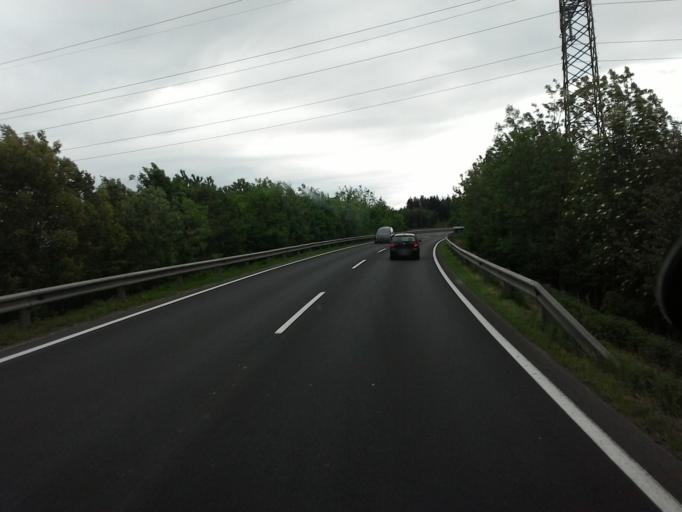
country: AT
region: Upper Austria
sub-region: Wels-Land
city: Sattledt
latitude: 48.0833
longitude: 14.0473
